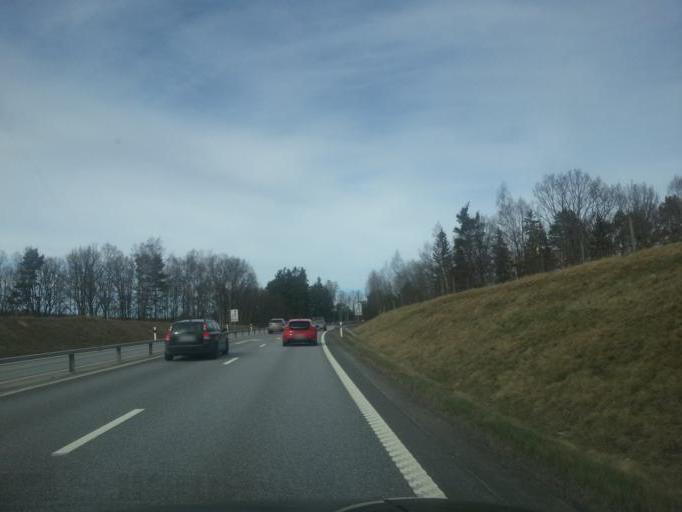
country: SE
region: Joenkoeping
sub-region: Jonkopings Kommun
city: Bankeryd
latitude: 57.8727
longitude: 14.1017
